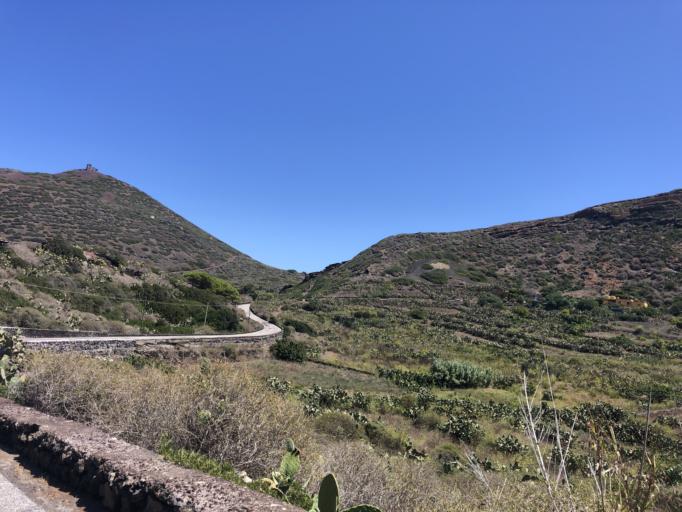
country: IT
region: Sicily
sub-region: Agrigento
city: Lampedusa
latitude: 35.8626
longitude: 12.8661
